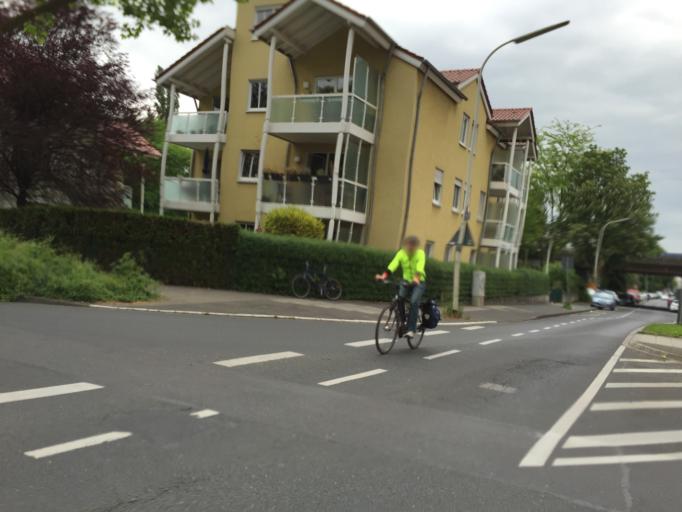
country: DE
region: North Rhine-Westphalia
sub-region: Regierungsbezirk Koln
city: Bonn
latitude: 50.7231
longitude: 7.0802
